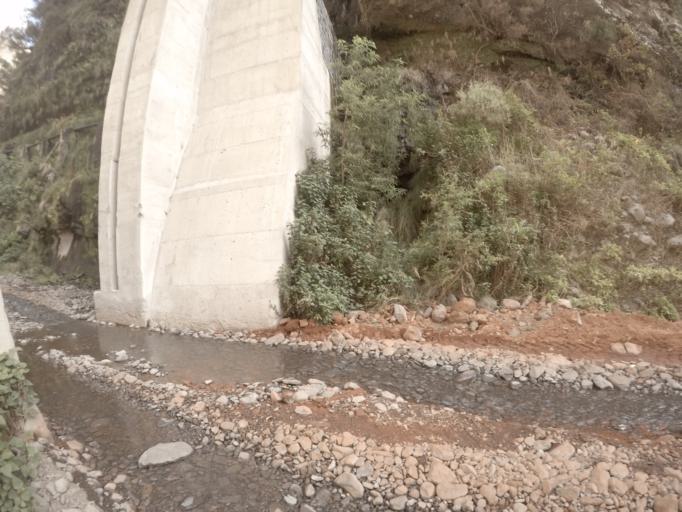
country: PT
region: Madeira
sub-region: Funchal
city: Nossa Senhora do Monte
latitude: 32.6972
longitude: -16.9185
